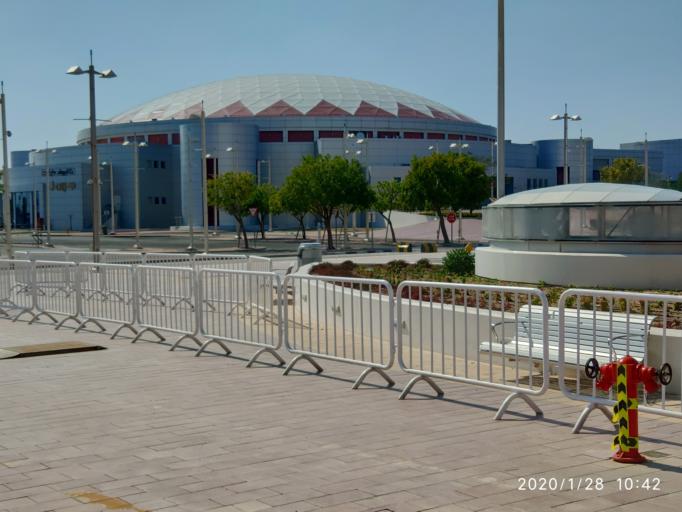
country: QA
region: Baladiyat ar Rayyan
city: Ar Rayyan
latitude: 25.2623
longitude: 51.4486
